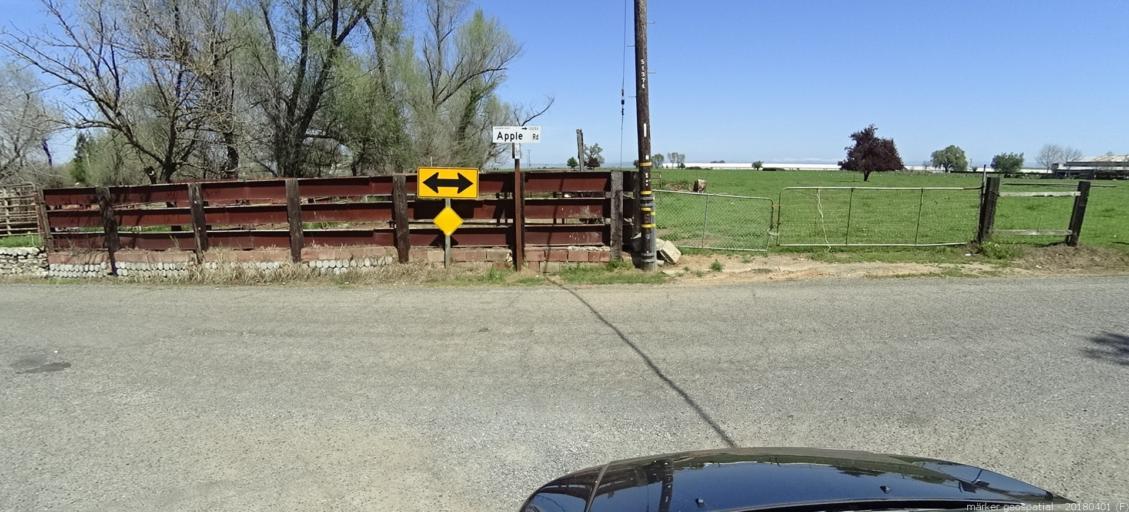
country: US
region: California
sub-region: Sacramento County
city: Rancho Murieta
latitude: 38.4501
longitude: -121.1700
